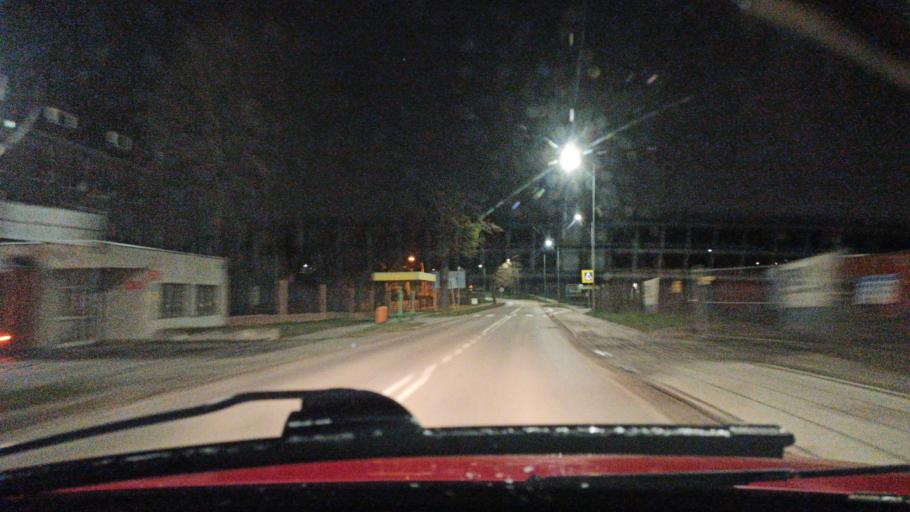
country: PL
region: Warmian-Masurian Voivodeship
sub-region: Powiat elblaski
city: Gronowo Gorne
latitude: 54.1560
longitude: 19.4400
